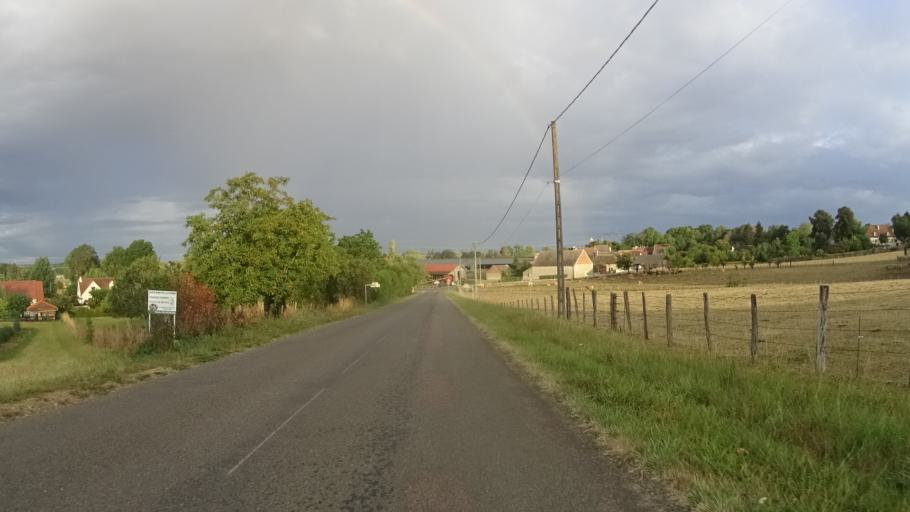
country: FR
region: Bourgogne
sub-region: Departement de Saone-et-Loire
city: Verdun-sur-le-Doubs
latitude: 46.9541
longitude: 5.0355
